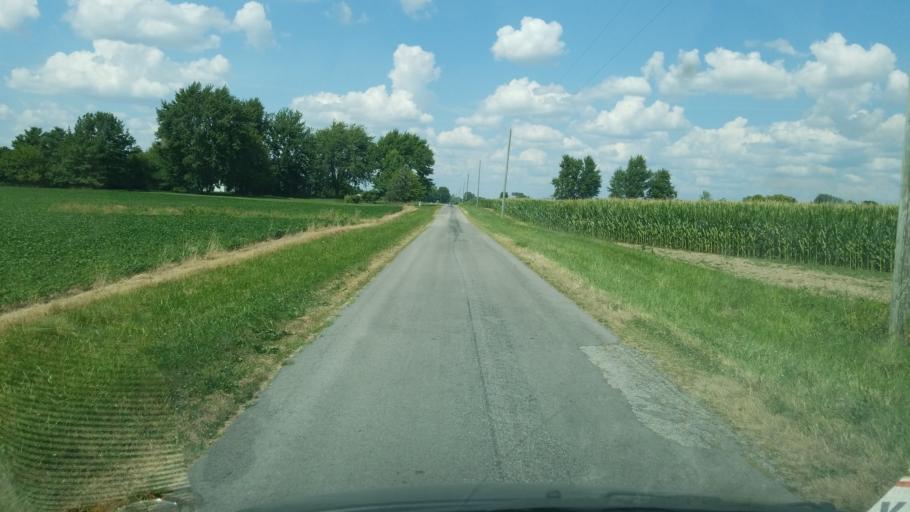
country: US
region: Ohio
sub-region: Union County
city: Richwood
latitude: 40.3918
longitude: -83.4745
